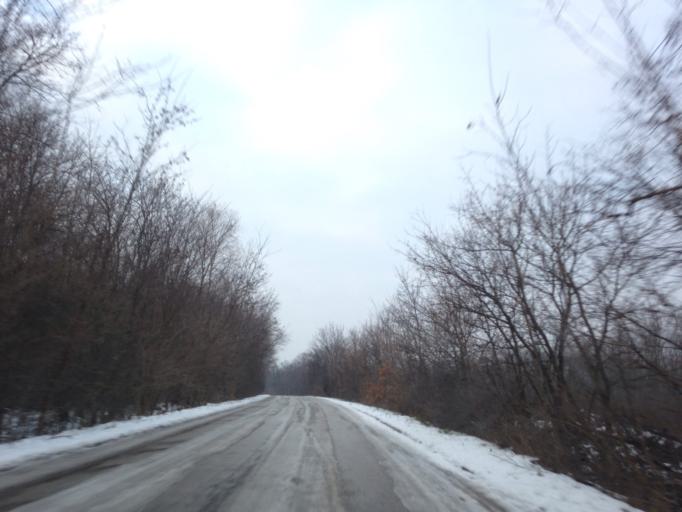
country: SK
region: Nitriansky
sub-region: Okres Nitra
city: Vrable
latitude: 48.0938
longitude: 18.3670
